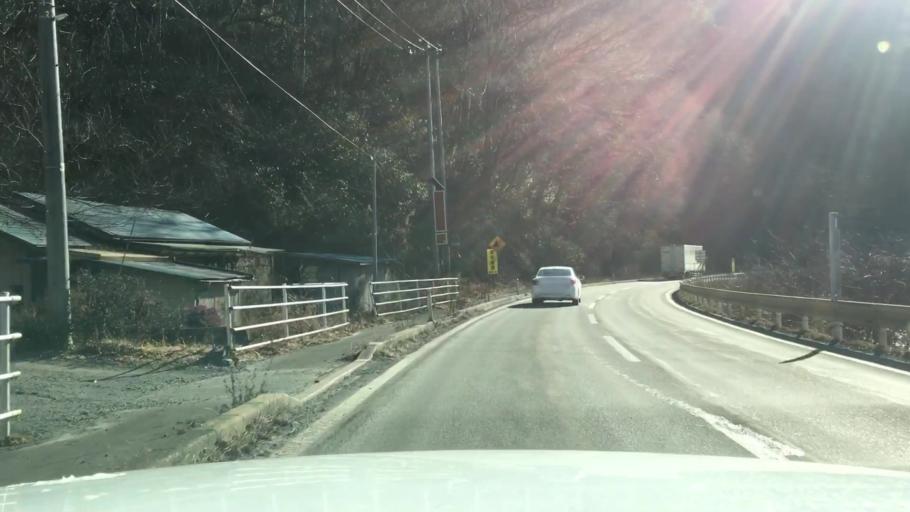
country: JP
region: Iwate
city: Miyako
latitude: 39.6080
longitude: 141.6519
